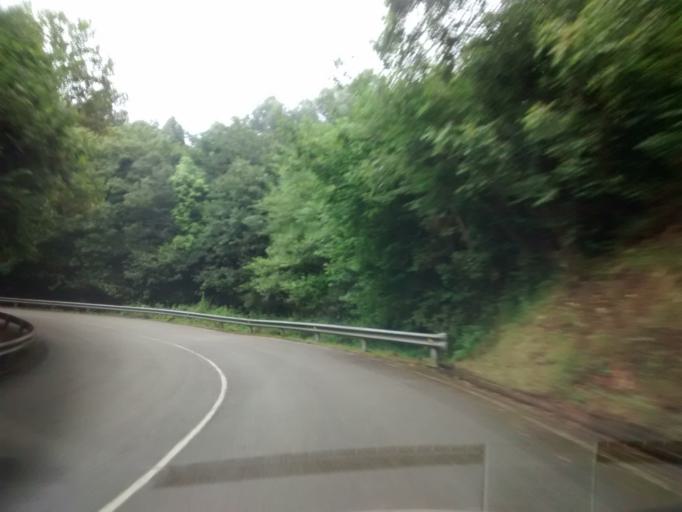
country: ES
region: Asturias
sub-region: Province of Asturias
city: Villaviciosa
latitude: 43.5388
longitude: -5.4026
